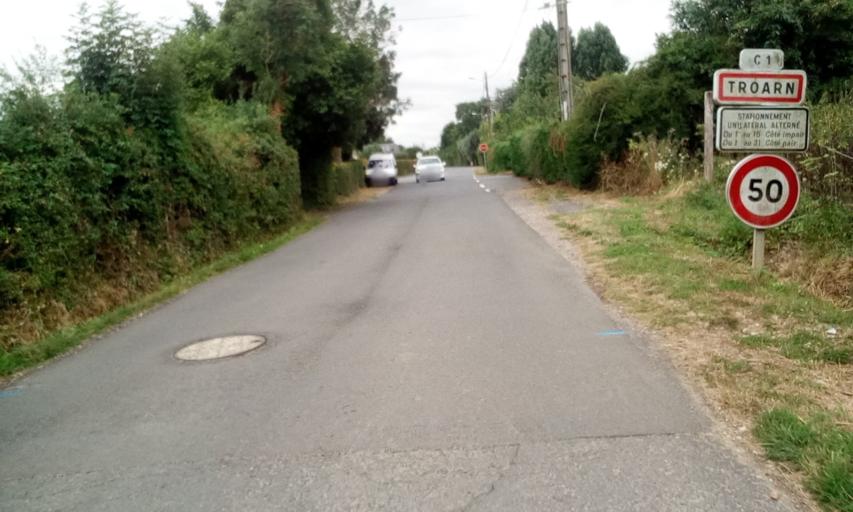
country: FR
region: Lower Normandy
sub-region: Departement du Calvados
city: Troarn
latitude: 49.1899
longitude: -0.1847
